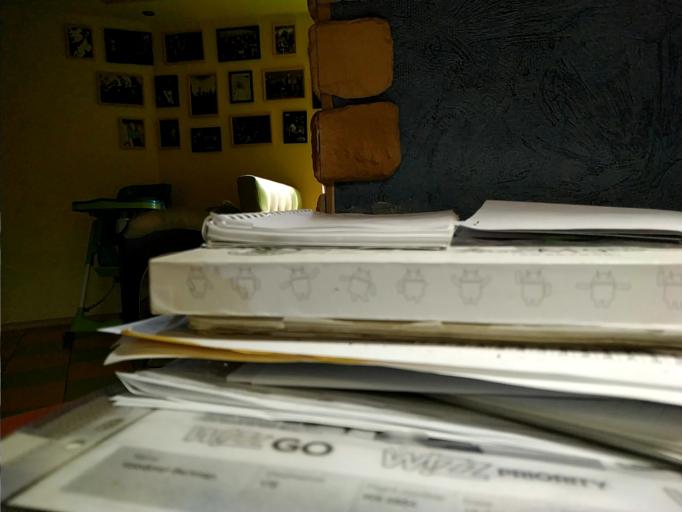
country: RU
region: Novgorod
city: Poddor'ye
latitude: 57.5672
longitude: 30.8525
